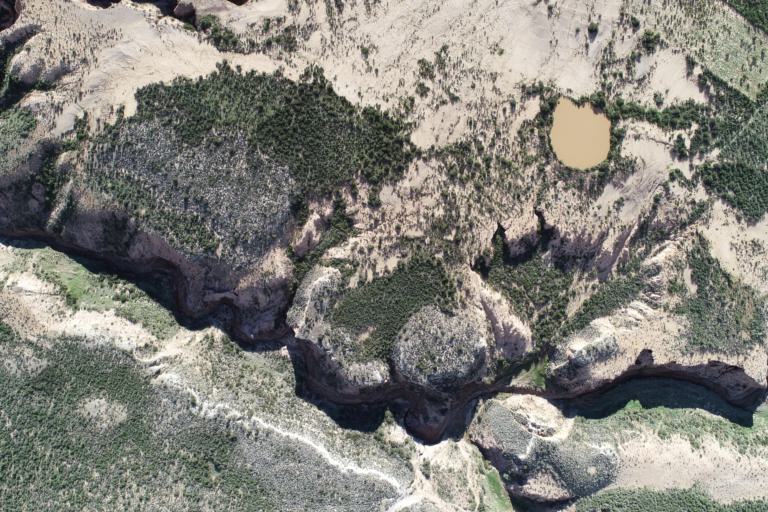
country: BO
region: La Paz
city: Patacamaya
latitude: -17.2960
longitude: -68.4899
